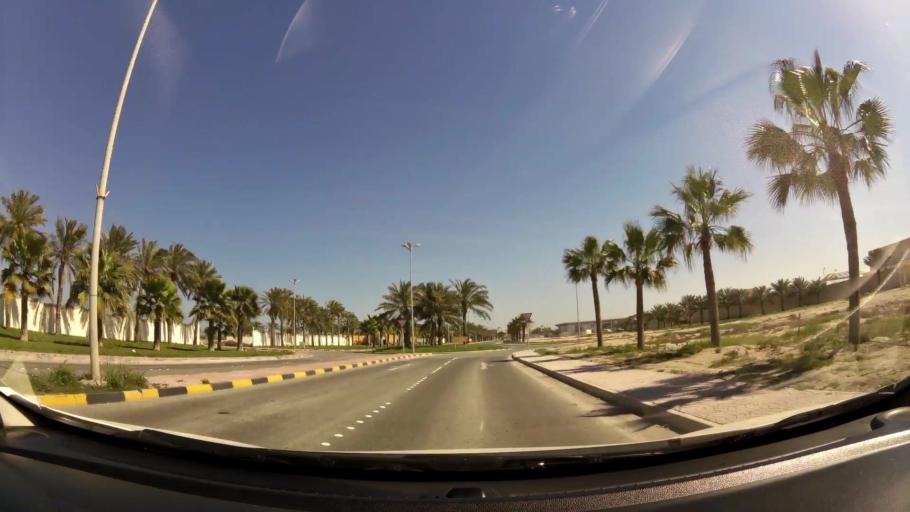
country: BH
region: Muharraq
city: Al Hadd
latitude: 26.2803
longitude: 50.6600
